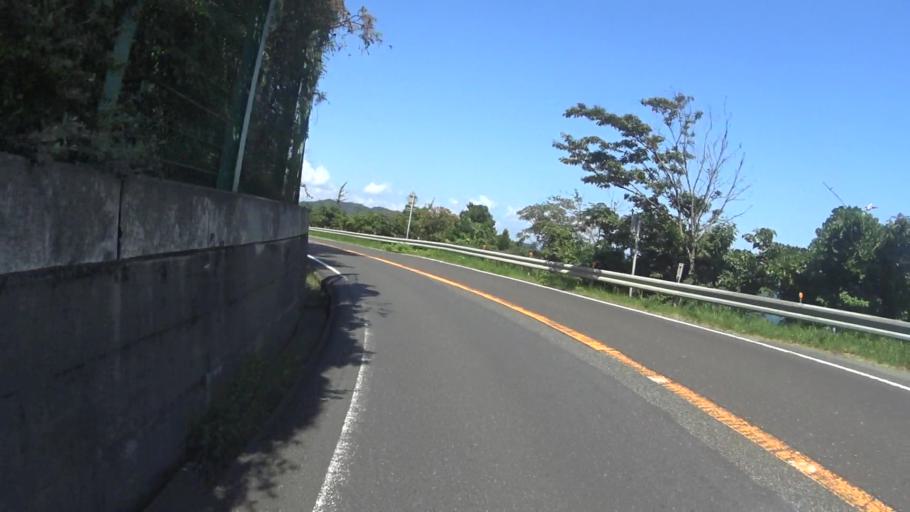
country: JP
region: Kyoto
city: Miyazu
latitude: 35.5324
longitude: 135.2693
